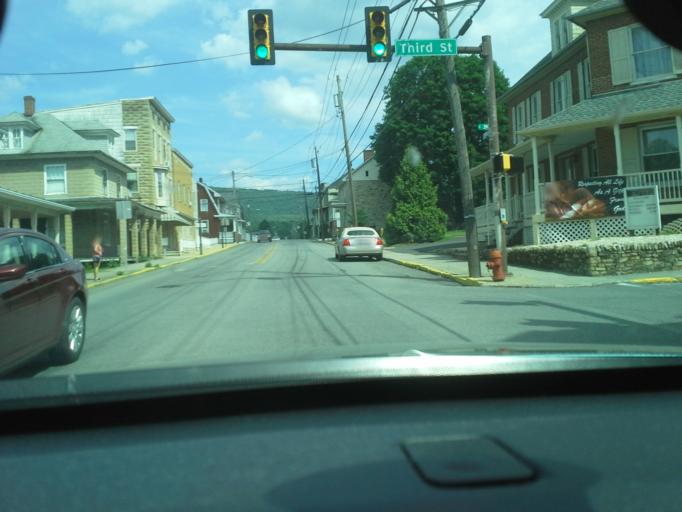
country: US
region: Pennsylvania
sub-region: Fulton County
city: McConnellsburg
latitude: 39.9320
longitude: -77.9975
